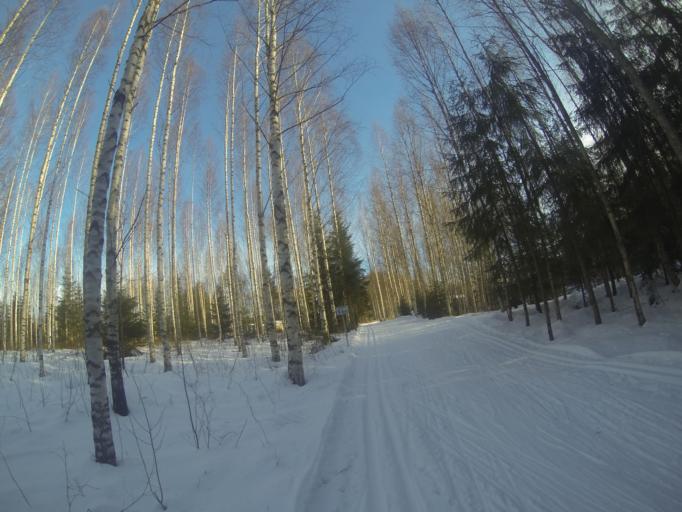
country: FI
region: Southern Savonia
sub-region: Savonlinna
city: Savonlinna
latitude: 61.9150
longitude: 28.9085
